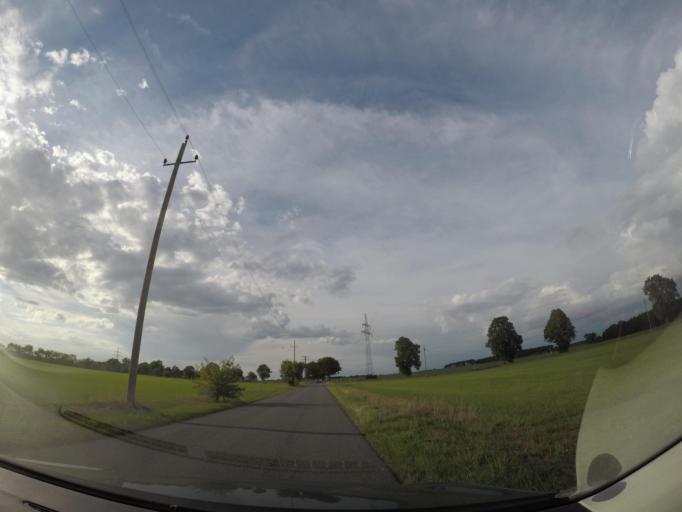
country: DE
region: Saxony-Anhalt
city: Kusey
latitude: 52.5673
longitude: 11.1281
